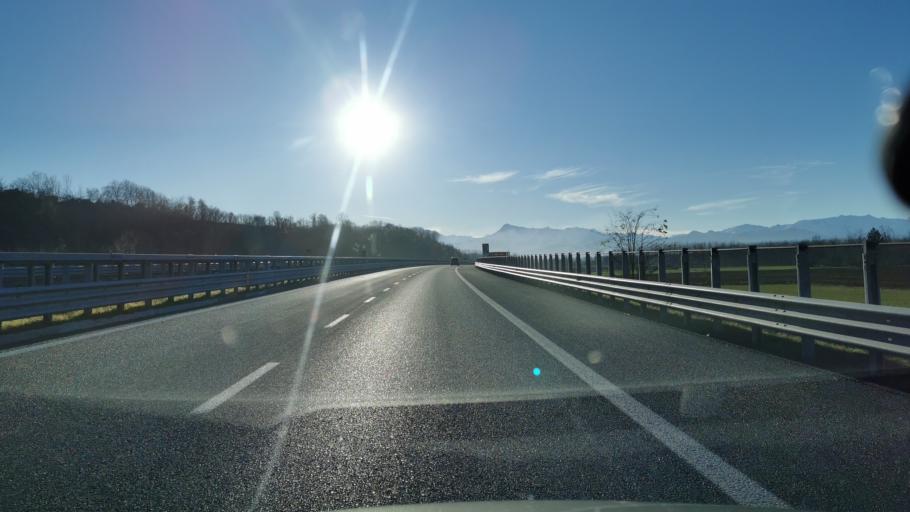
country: IT
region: Piedmont
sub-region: Provincia di Cuneo
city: Castelletto Stura
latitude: 44.4443
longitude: 7.6338
